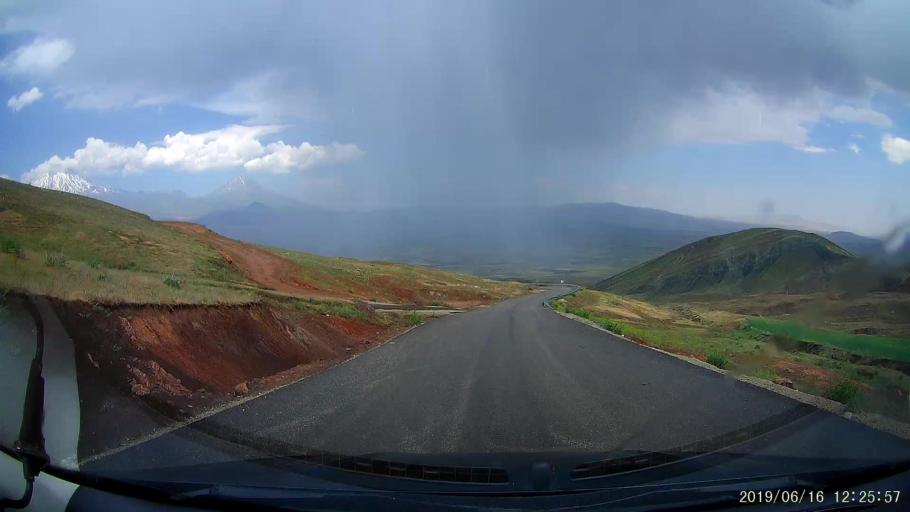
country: TR
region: Agri
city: Dogubayazit
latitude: 39.4443
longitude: 44.2351
